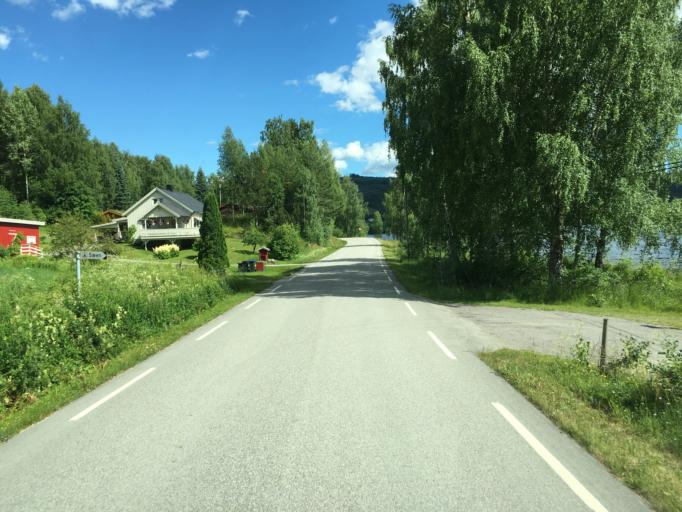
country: NO
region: Oppland
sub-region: Sondre Land
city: Hov
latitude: 60.5990
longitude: 10.3117
